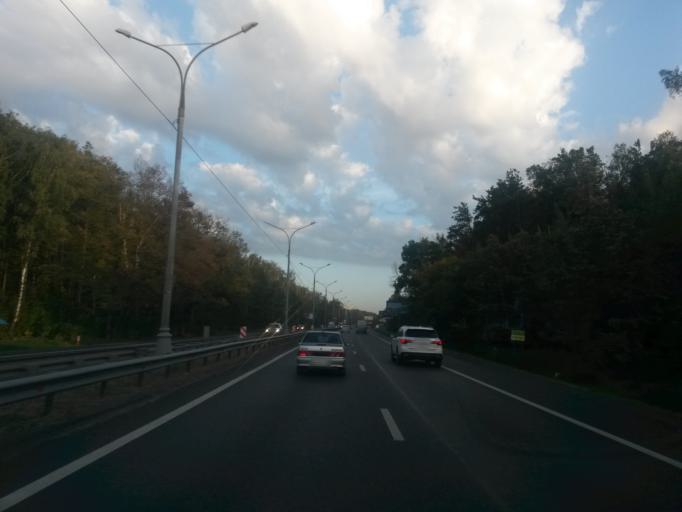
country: RU
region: Moskovskaya
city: Petrovskaya
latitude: 55.5523
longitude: 37.7864
